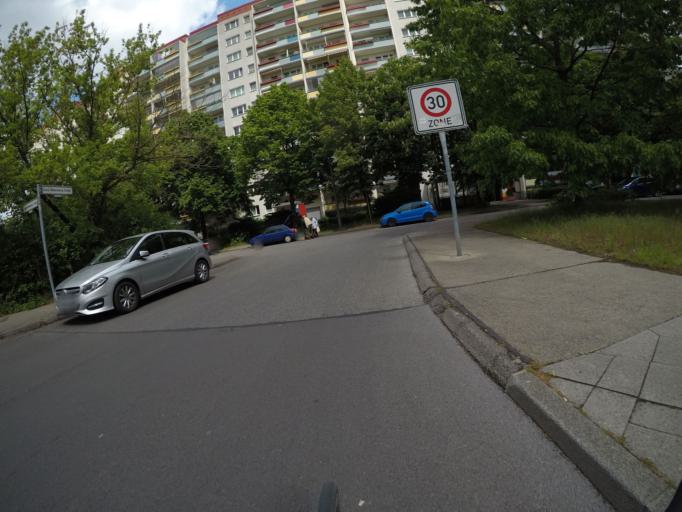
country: DE
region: Berlin
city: Marzahn
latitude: 52.5486
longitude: 13.5560
